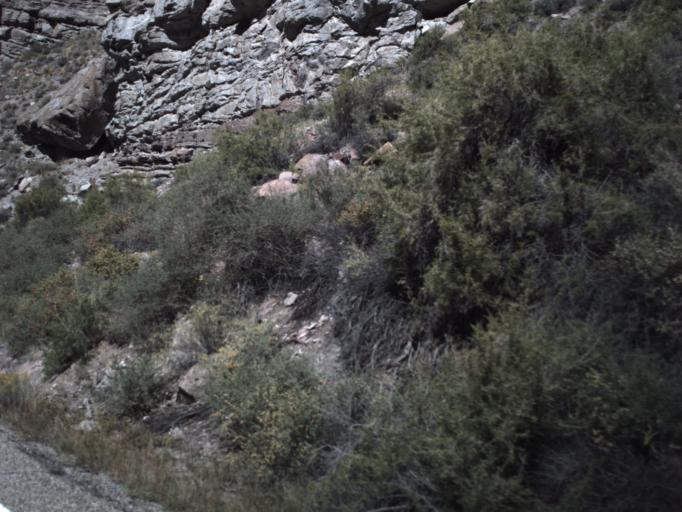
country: US
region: Utah
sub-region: Piute County
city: Junction
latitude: 38.1926
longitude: -112.1052
